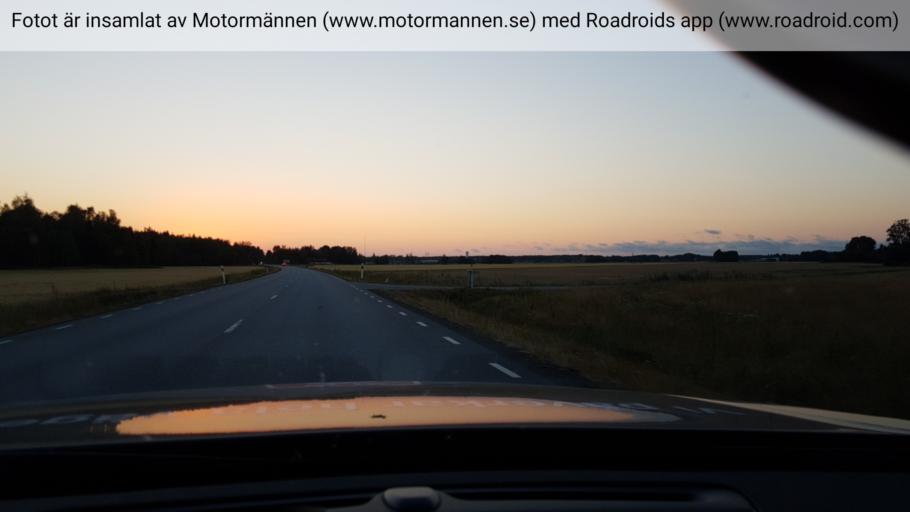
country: SE
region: Uppsala
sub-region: Heby Kommun
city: OEstervala
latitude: 60.1616
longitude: 17.2026
